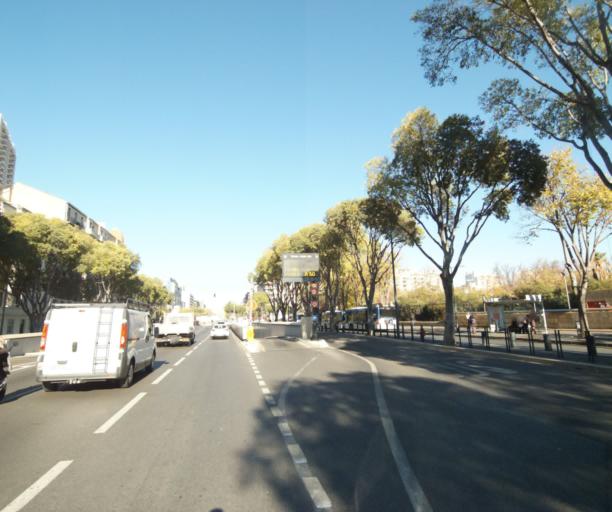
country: FR
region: Provence-Alpes-Cote d'Azur
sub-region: Departement des Bouches-du-Rhone
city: Marseille 08
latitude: 43.2711
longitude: 5.3922
